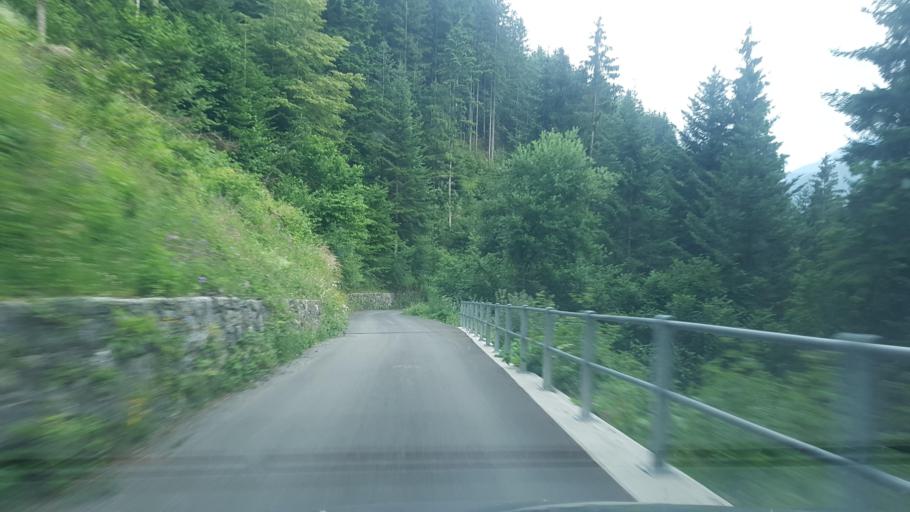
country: IT
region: Friuli Venezia Giulia
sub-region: Provincia di Udine
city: Paularo
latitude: 46.5497
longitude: 13.1231
